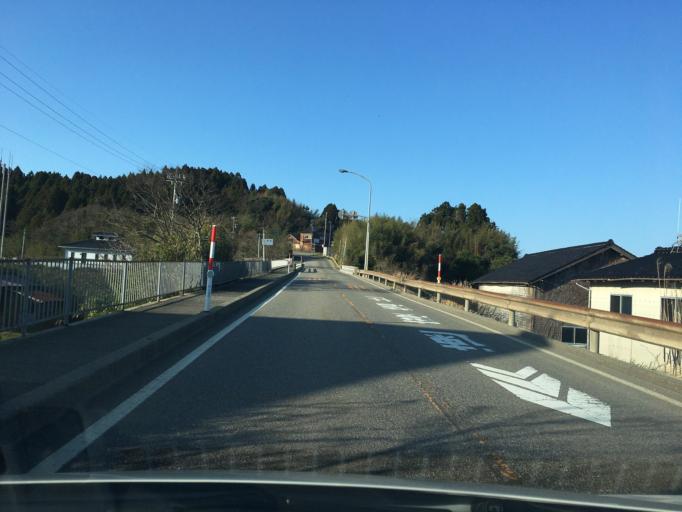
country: JP
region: Ishikawa
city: Nanao
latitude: 36.9782
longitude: 137.0499
